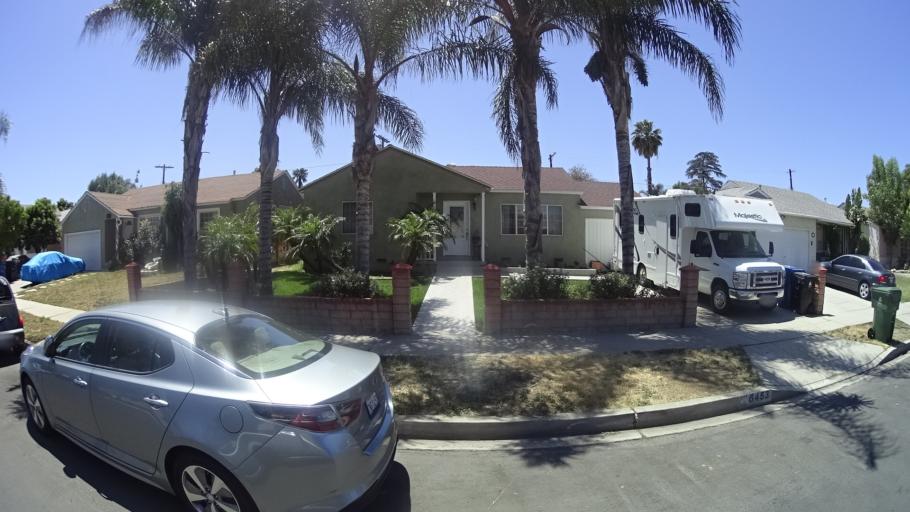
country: US
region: California
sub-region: Los Angeles County
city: Northridge
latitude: 34.1882
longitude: -118.5225
